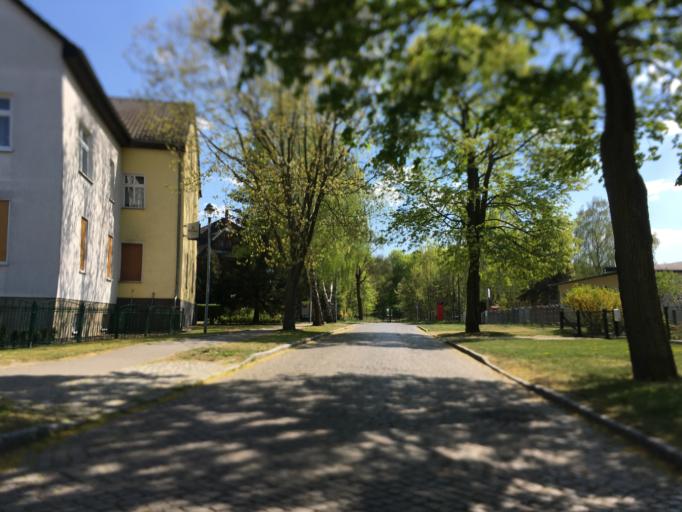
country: DE
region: Brandenburg
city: Werneuchen
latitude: 52.6196
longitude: 13.6767
